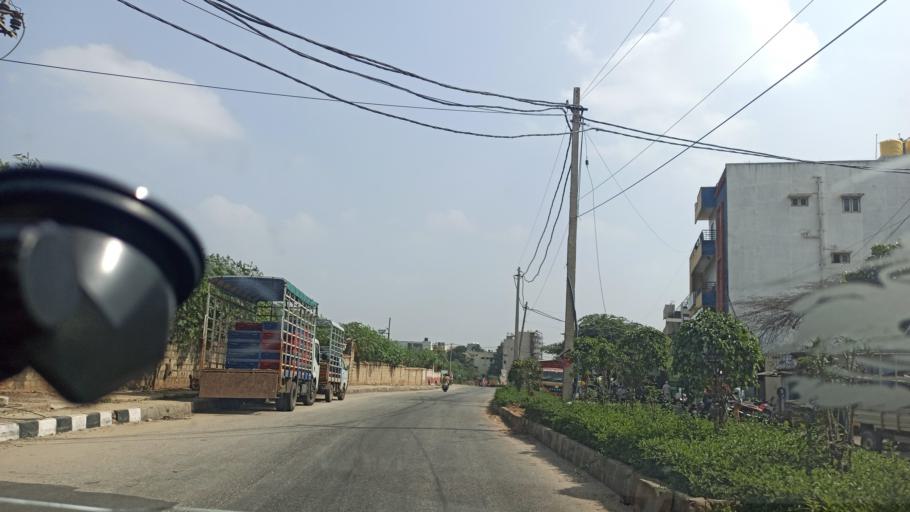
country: IN
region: Karnataka
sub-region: Bangalore Urban
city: Yelahanka
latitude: 13.0730
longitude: 77.6004
